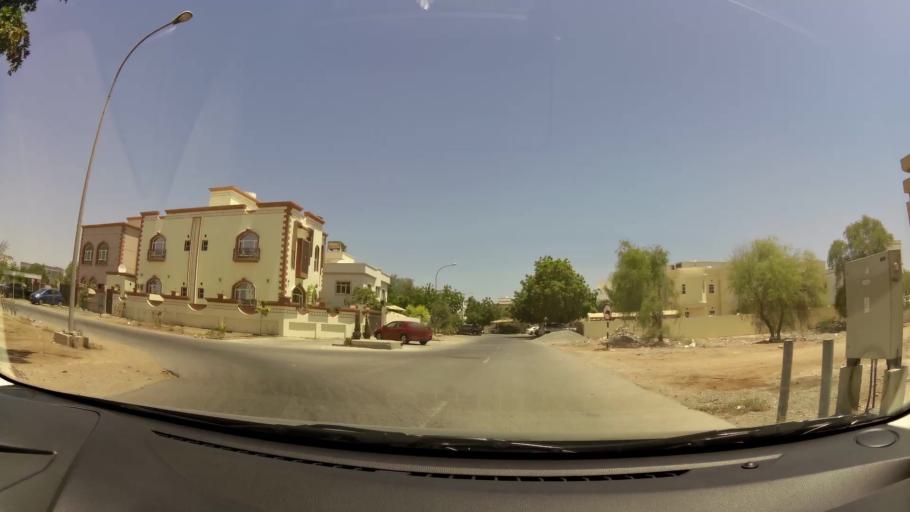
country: OM
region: Muhafazat Masqat
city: As Sib al Jadidah
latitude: 23.6291
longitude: 58.2405
